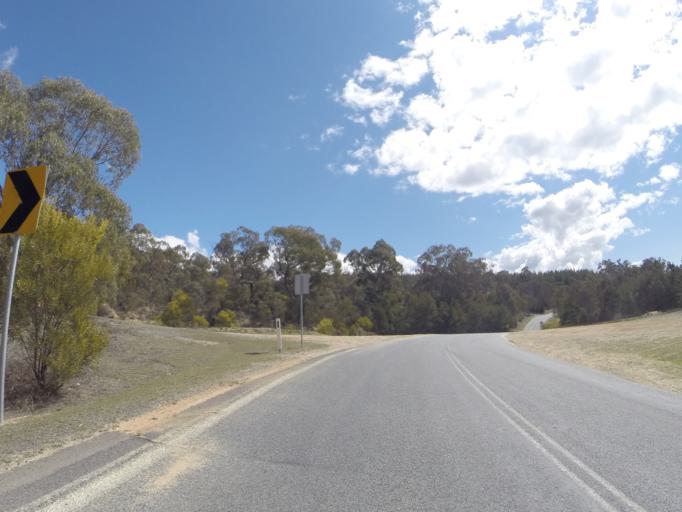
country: AU
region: Australian Capital Territory
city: Macquarie
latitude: -35.3611
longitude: 148.9477
